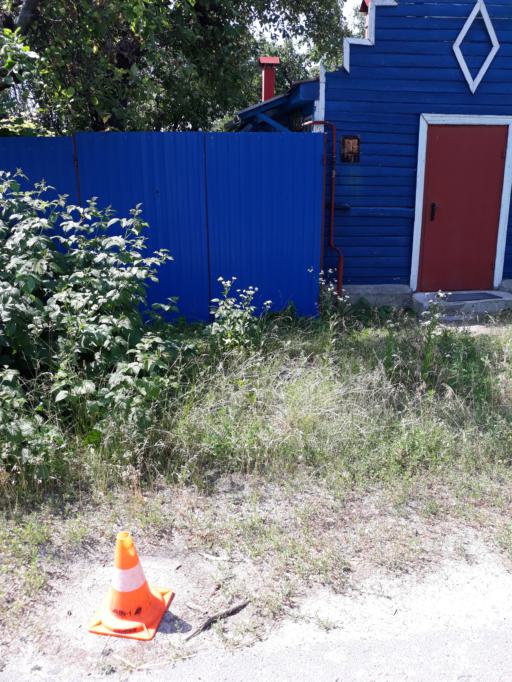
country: RU
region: Voronezj
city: Voronezh
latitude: 51.6837
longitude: 39.2250
